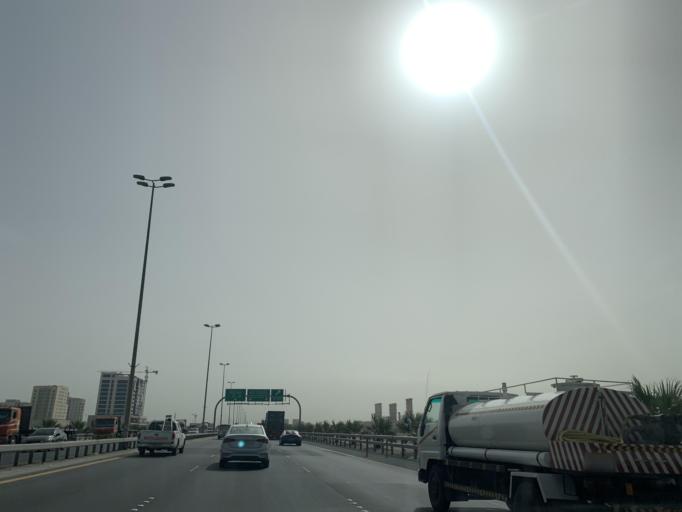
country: BH
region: Muharraq
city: Al Hadd
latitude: 26.2251
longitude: 50.6492
